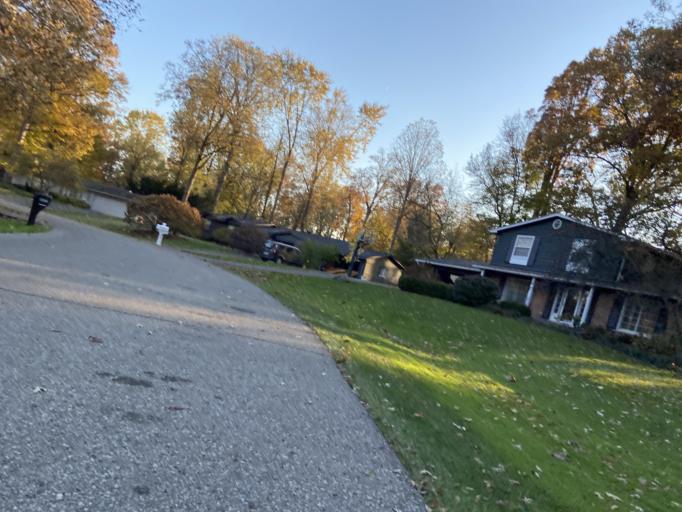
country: US
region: Michigan
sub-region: Oakland County
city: Franklin
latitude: 42.5379
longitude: -83.3390
